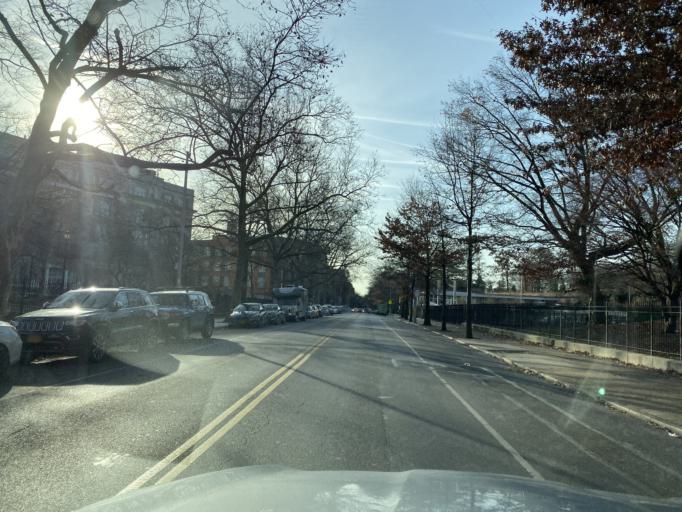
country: US
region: New York
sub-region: Kings County
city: Brooklyn
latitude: 40.6708
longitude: -73.9624
